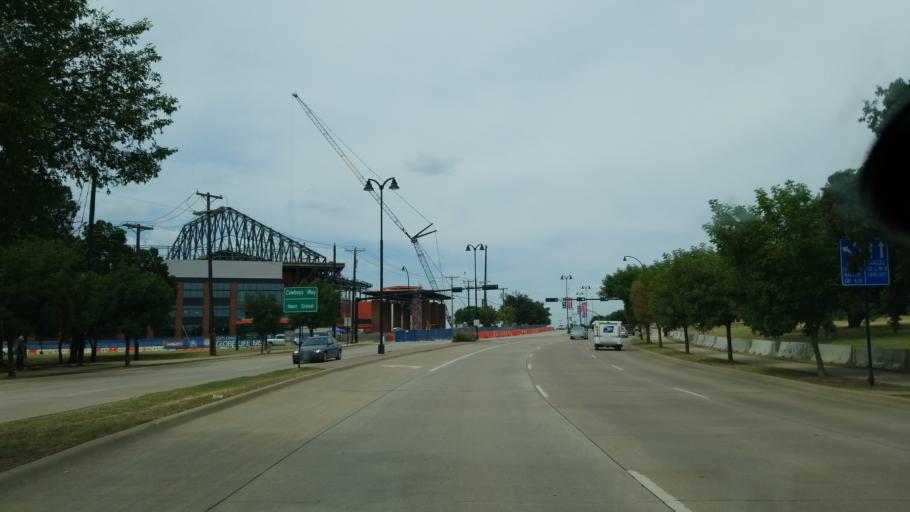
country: US
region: Texas
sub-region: Tarrant County
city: Arlington
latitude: 32.7445
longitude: -97.0836
